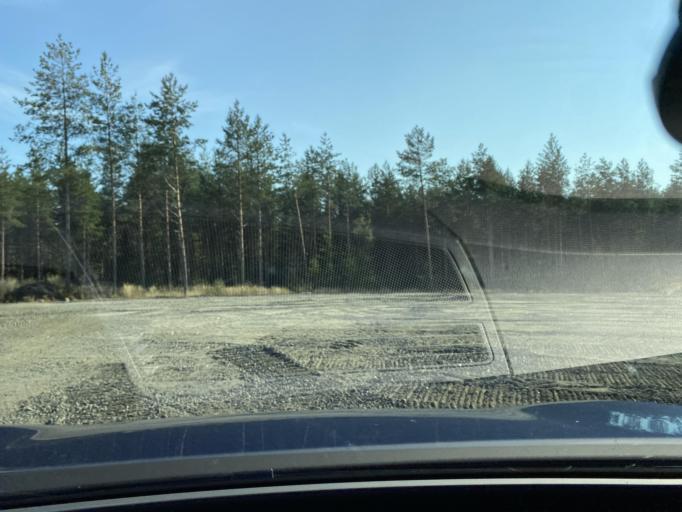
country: FI
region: Kymenlaakso
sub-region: Kouvola
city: Iitti
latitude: 60.8842
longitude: 26.4835
